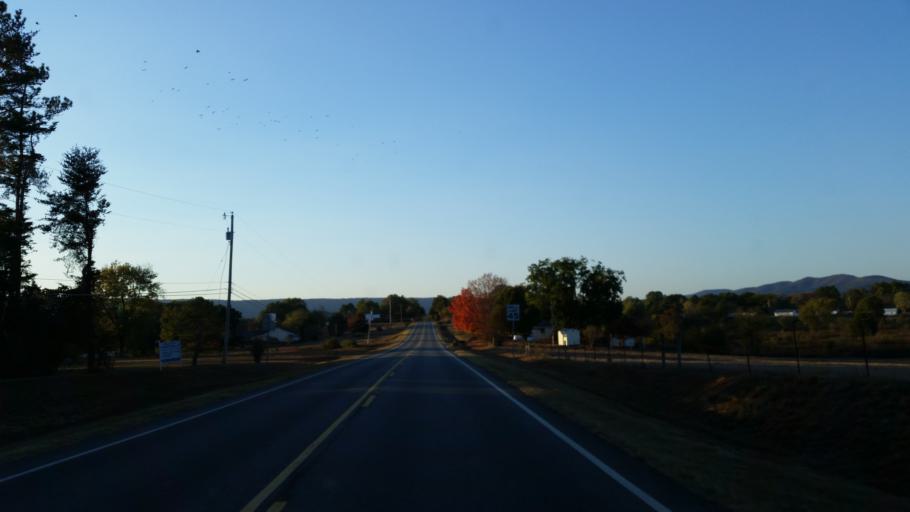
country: US
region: Georgia
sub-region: Gordon County
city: Calhoun
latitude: 34.5522
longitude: -85.0059
